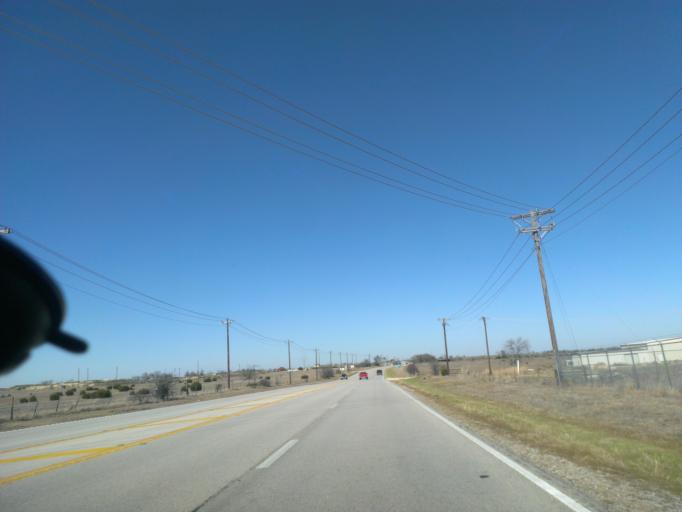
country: US
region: Texas
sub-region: Williamson County
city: Florence
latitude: 30.8386
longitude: -97.9030
